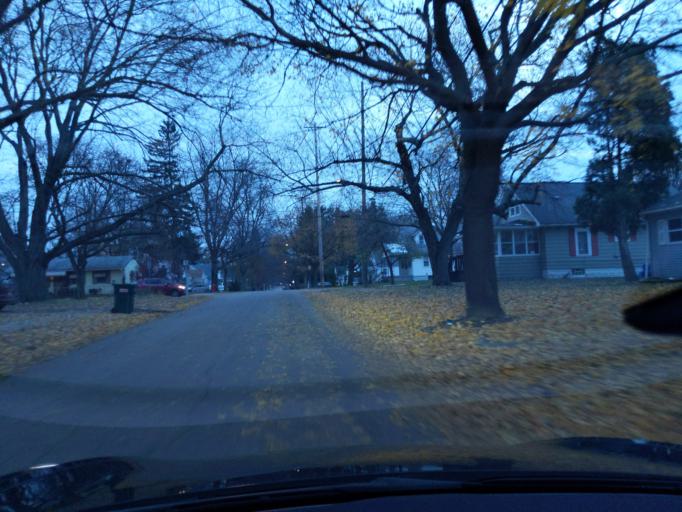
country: US
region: Michigan
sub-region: Ingham County
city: Lansing
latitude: 42.7022
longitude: -84.5591
